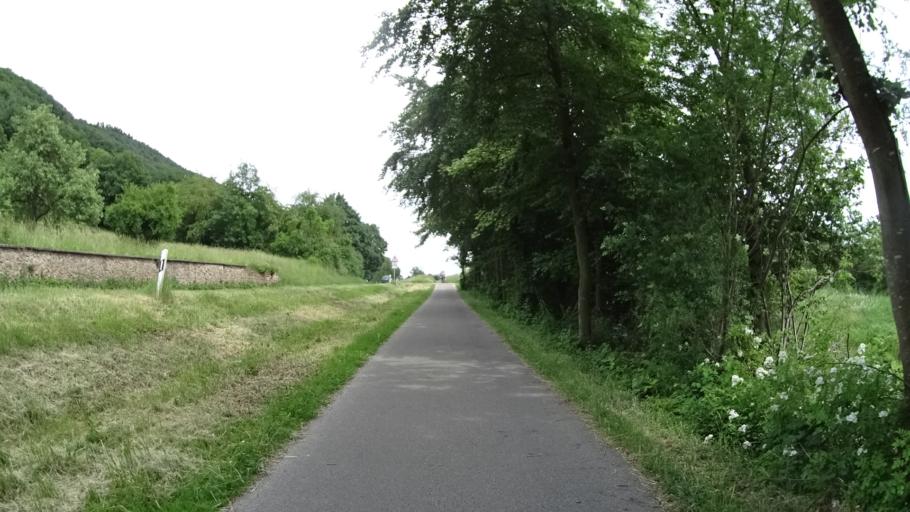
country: DE
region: Bavaria
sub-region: Upper Palatinate
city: Donaustauf
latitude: 49.0240
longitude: 12.2482
